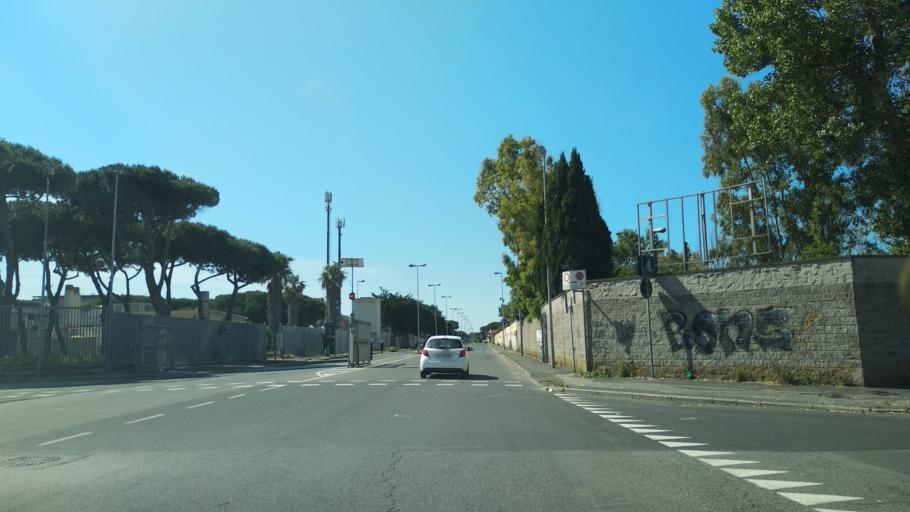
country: IT
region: Tuscany
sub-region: Provincia di Livorno
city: Livorno
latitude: 43.5260
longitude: 10.3157
